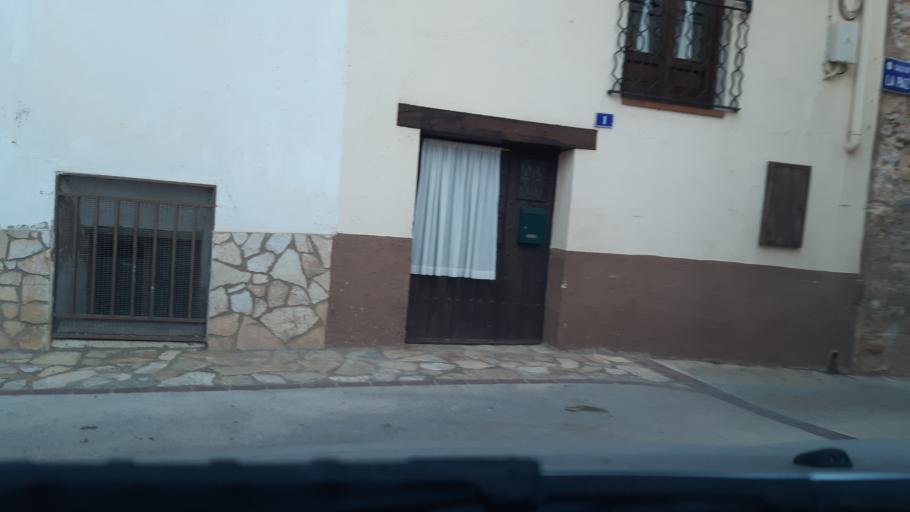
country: ES
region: Aragon
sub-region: Provincia de Teruel
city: Valderrobres
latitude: 40.8320
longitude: 0.1834
